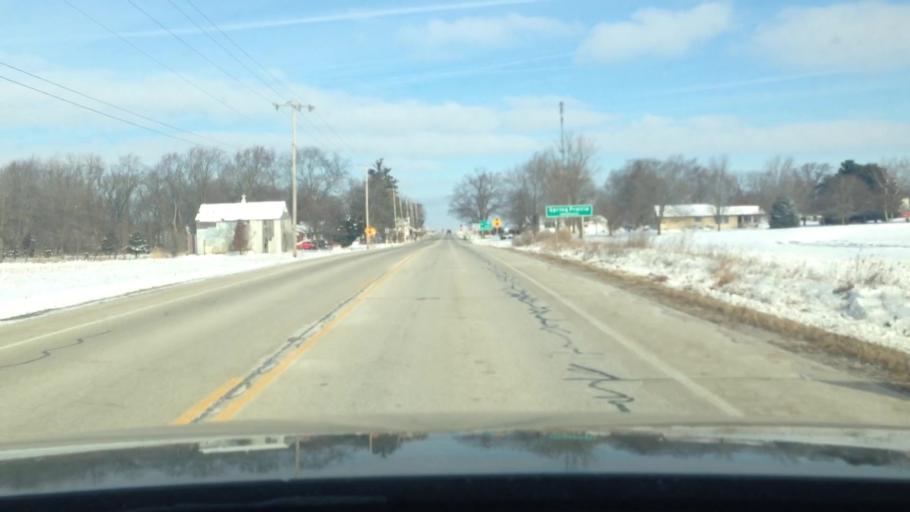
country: US
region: Wisconsin
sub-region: Walworth County
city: East Troy
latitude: 42.6883
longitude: -88.4046
